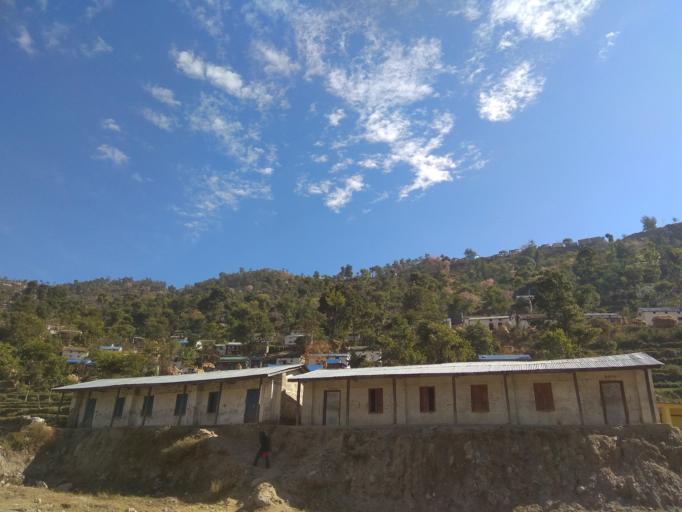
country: NP
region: Far Western
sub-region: Seti Zone
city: Achham
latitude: 29.2399
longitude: 81.6329
